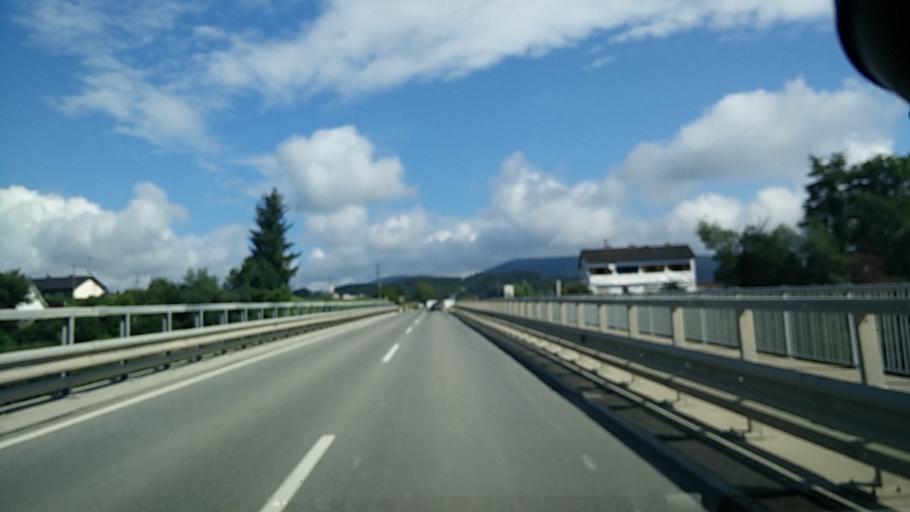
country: AT
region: Carinthia
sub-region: Politischer Bezirk Volkermarkt
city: Gallizien
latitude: 46.6204
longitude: 14.5472
